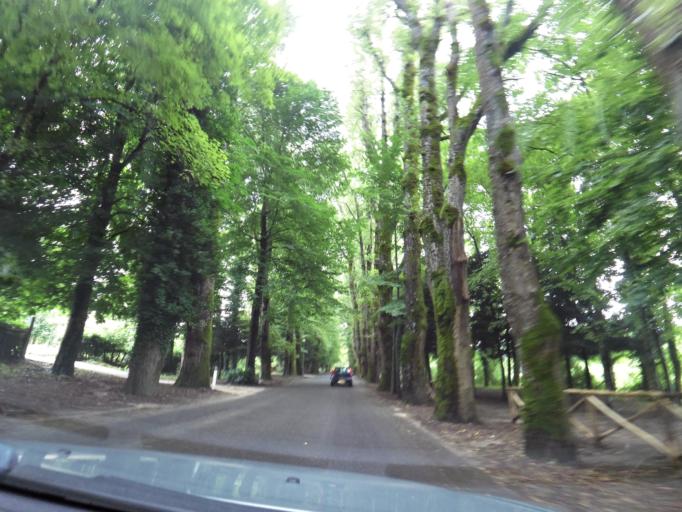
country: IT
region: Calabria
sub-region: Provincia di Vibo-Valentia
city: Serra San Bruno
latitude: 38.5692
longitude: 16.3227
